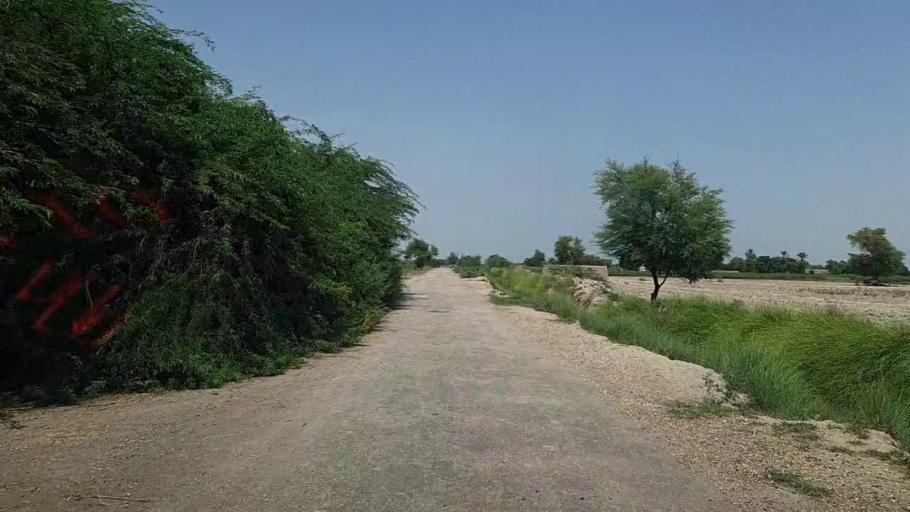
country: PK
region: Sindh
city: Pad Idan
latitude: 26.7554
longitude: 68.3174
